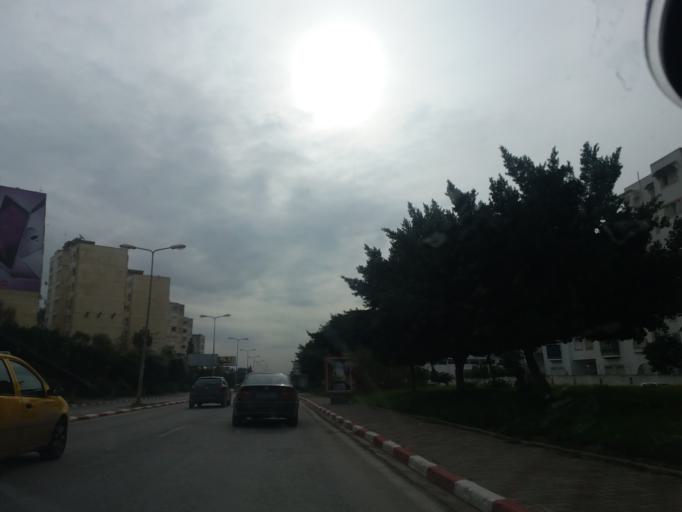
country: TN
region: Tunis
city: Tunis
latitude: 36.8454
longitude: 10.1625
